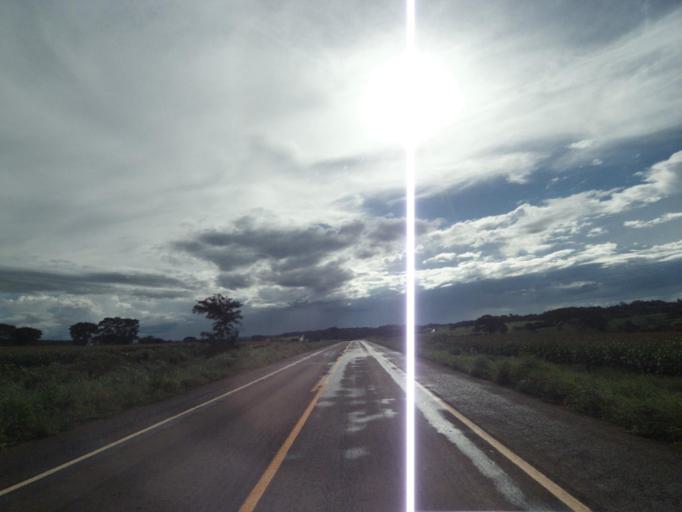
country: BR
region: Goias
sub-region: Jaragua
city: Jaragua
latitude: -15.9057
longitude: -49.5505
